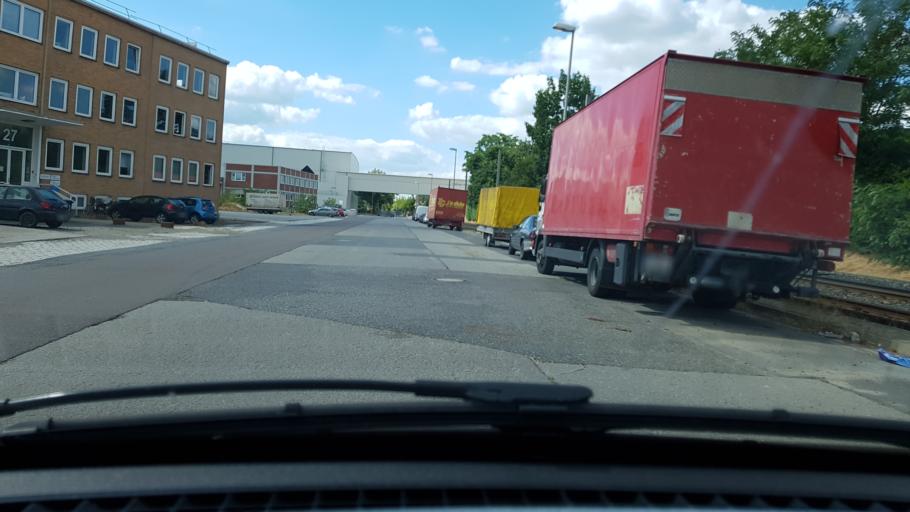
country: DE
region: Lower Saxony
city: Braunschweig
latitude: 52.2530
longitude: 10.5559
